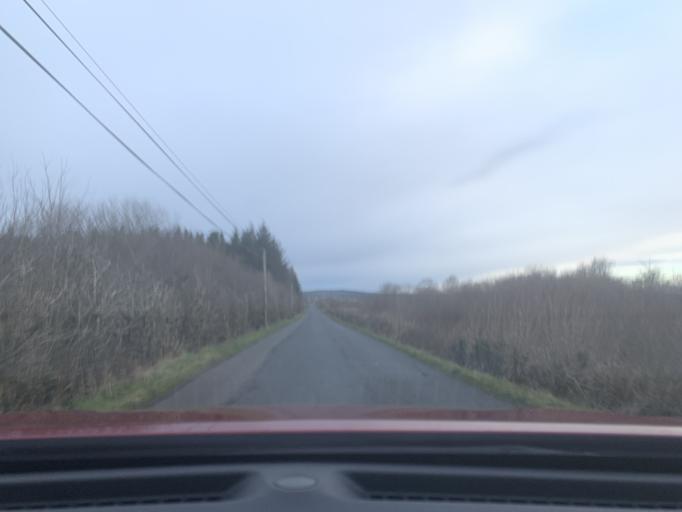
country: IE
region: Connaught
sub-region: Roscommon
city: Ballaghaderreen
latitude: 53.8823
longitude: -8.5655
